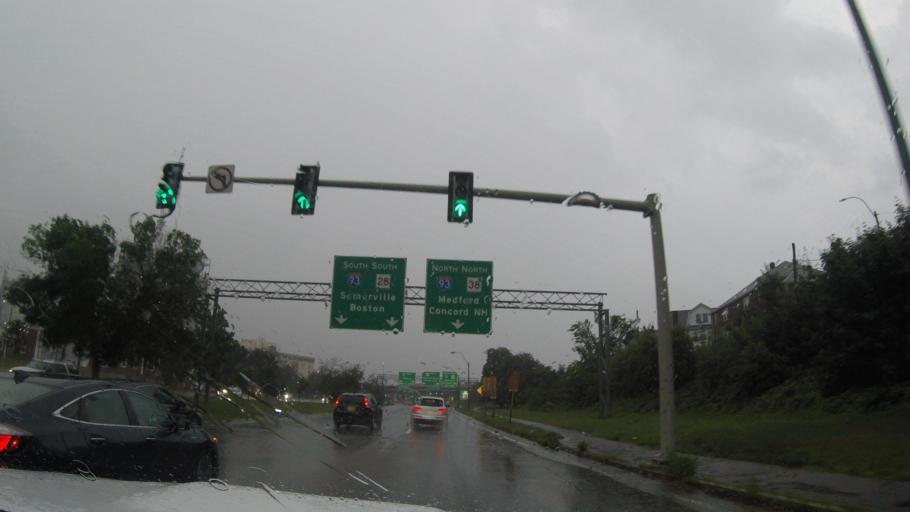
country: US
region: Massachusetts
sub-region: Middlesex County
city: Somerville
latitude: 42.3967
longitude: -71.0850
